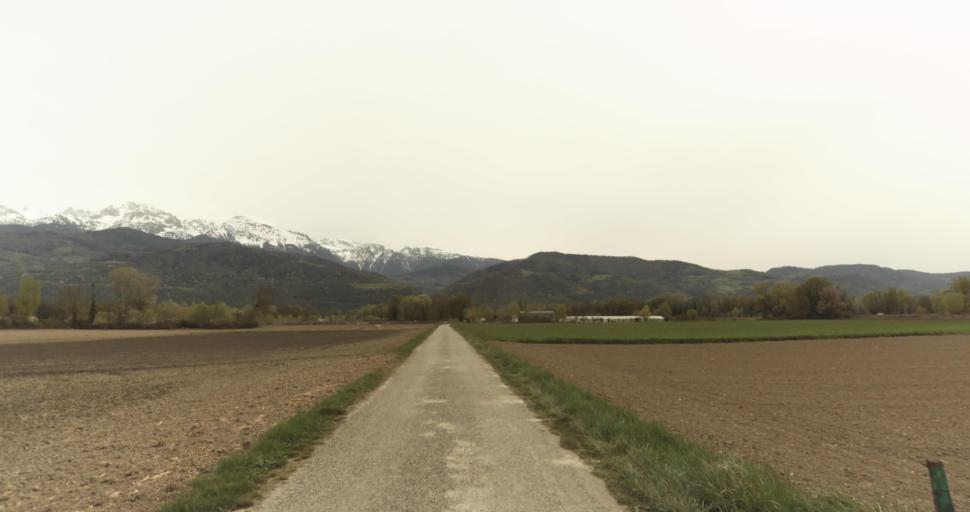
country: FR
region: Rhone-Alpes
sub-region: Departement de l'Isere
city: Montbonnot-Saint-Martin
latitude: 45.2234
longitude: 5.8249
